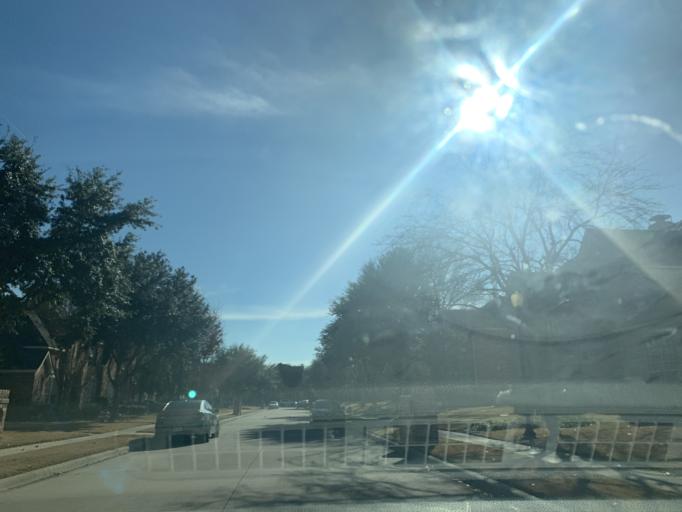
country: US
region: Texas
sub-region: Denton County
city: The Colony
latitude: 33.0558
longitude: -96.8161
